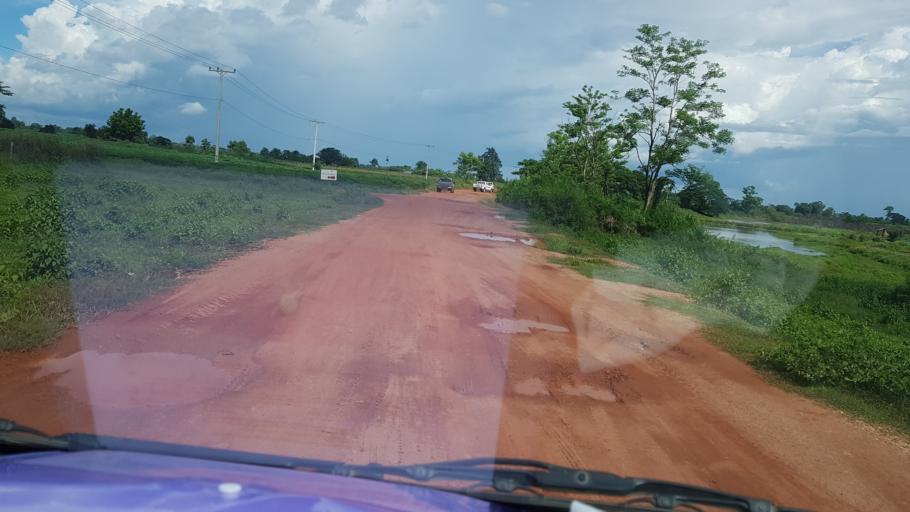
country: LA
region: Vientiane
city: Vientiane
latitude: 18.2355
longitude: 102.5612
